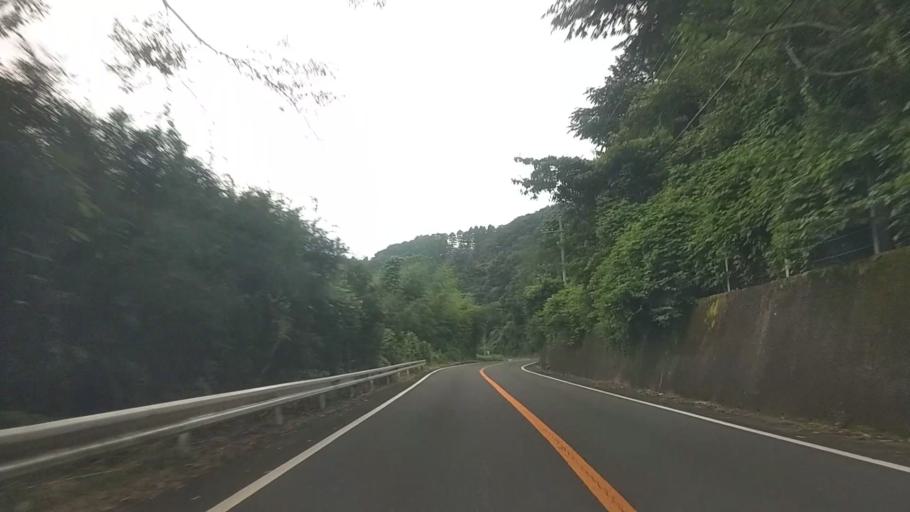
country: JP
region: Chiba
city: Kawaguchi
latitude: 35.2360
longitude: 140.0739
